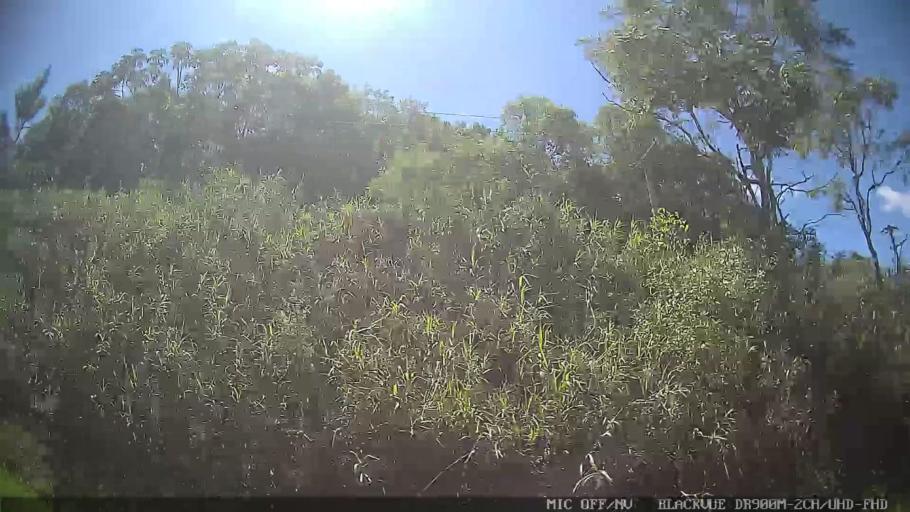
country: BR
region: Sao Paulo
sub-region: Mogi das Cruzes
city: Mogi das Cruzes
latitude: -23.6127
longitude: -46.1768
